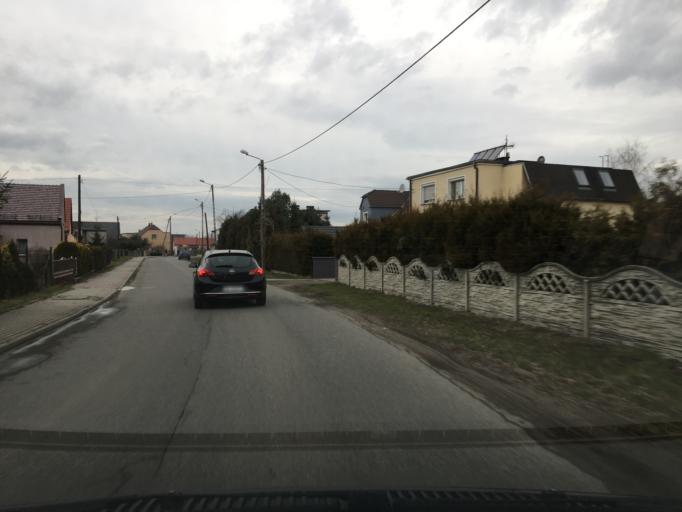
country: PL
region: Opole Voivodeship
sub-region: Powiat kedzierzynsko-kozielski
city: Kozle
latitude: 50.3543
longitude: 18.1322
